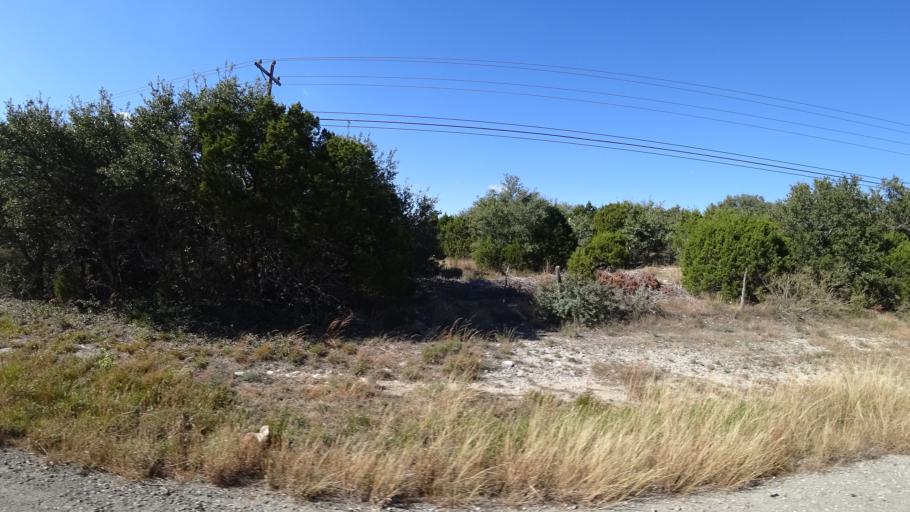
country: US
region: Texas
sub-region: Travis County
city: Shady Hollow
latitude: 30.2159
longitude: -97.8956
